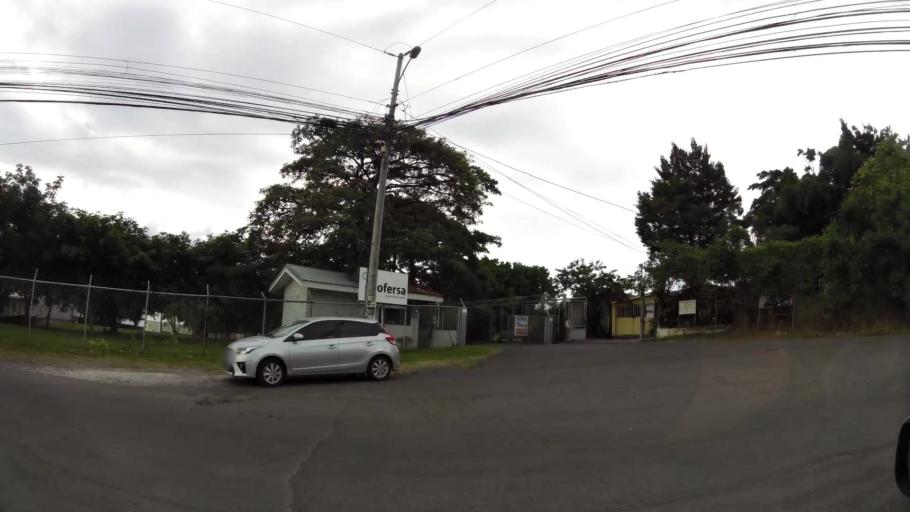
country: CR
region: Heredia
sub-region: Canton de Belen
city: San Antonio
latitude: 9.9619
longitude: -84.1912
